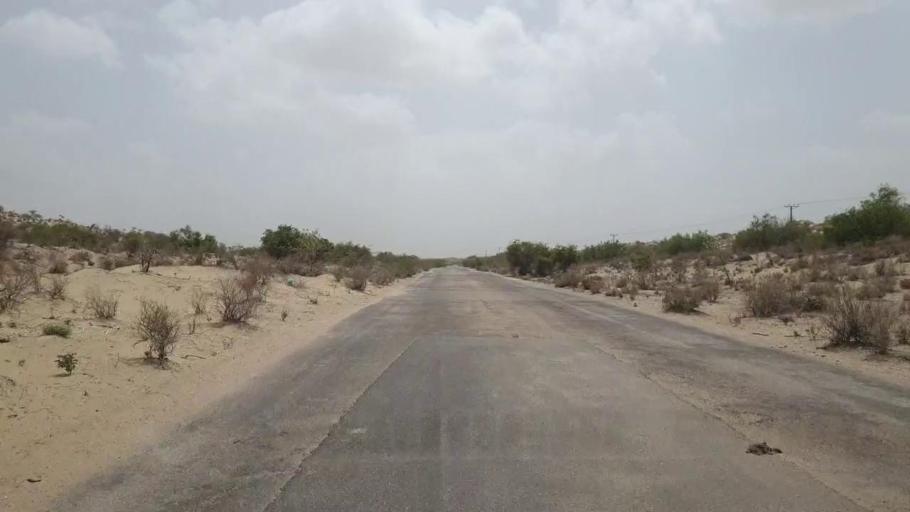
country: PK
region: Sindh
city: Diplo
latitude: 24.4038
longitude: 69.4761
